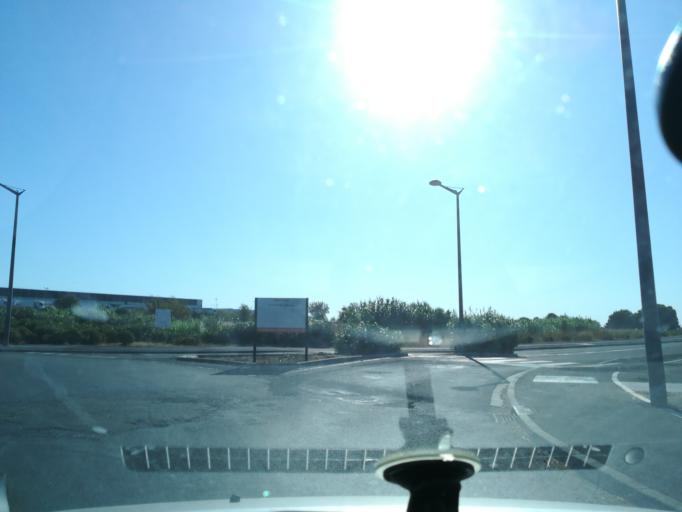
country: FR
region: Languedoc-Roussillon
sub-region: Departement de l'Herault
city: Villeneuve-les-Beziers
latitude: 43.3369
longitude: 3.2841
